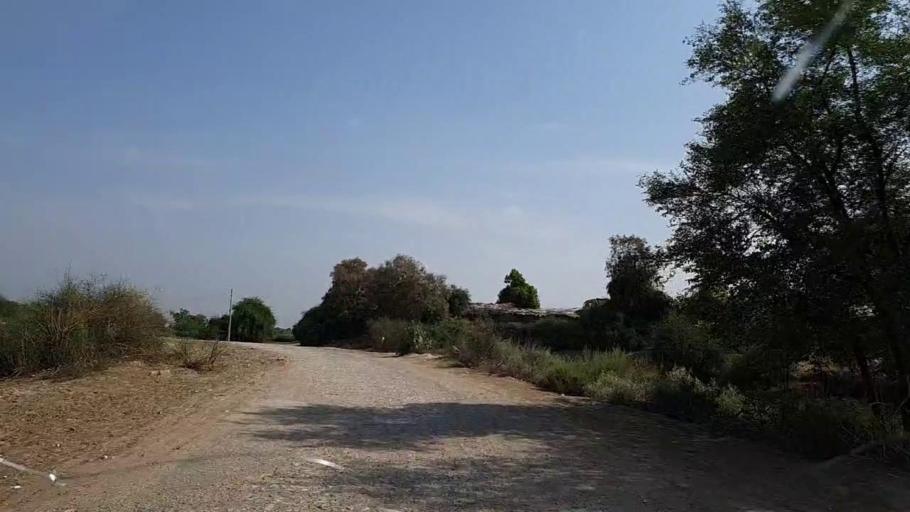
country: PK
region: Sindh
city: Khanpur
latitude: 27.7298
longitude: 69.3585
